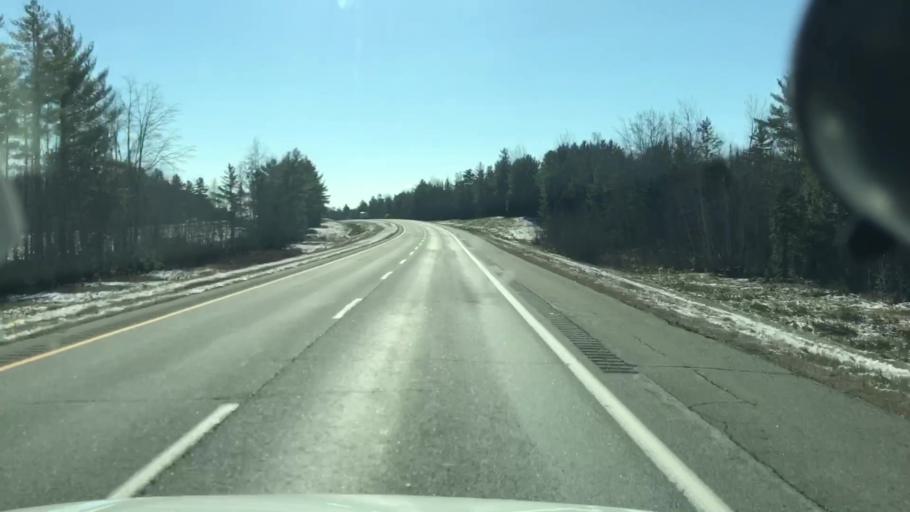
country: US
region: Maine
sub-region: Penobscot County
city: Howland
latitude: 45.2638
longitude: -68.6807
